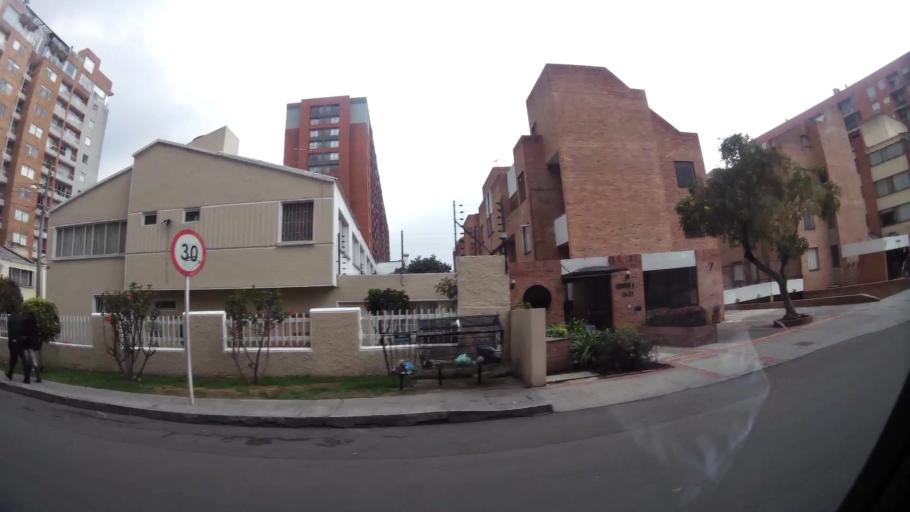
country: CO
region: Bogota D.C.
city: Barrio San Luis
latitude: 4.7232
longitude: -74.0402
